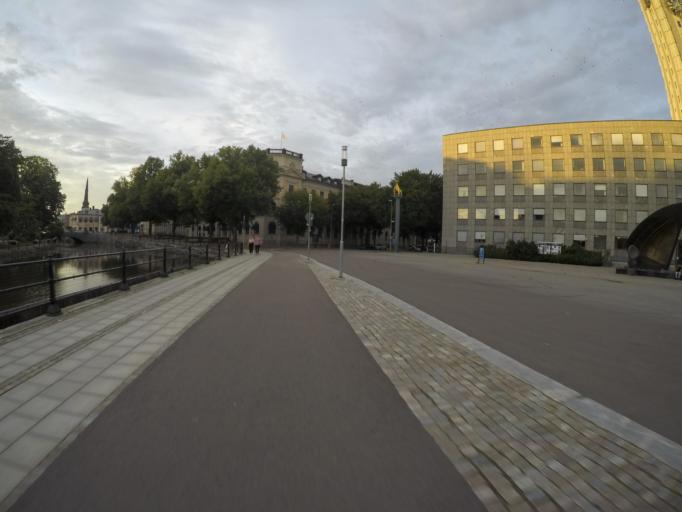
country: SE
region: Vaestmanland
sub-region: Vasteras
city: Vasteras
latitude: 59.6082
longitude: 16.5449
